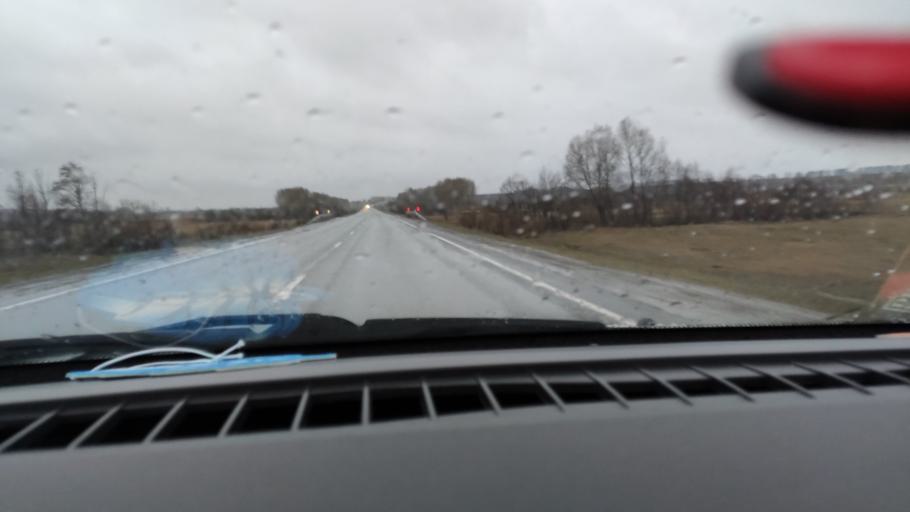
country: RU
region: Tatarstan
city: Mendeleyevsk
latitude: 55.9671
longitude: 52.3166
